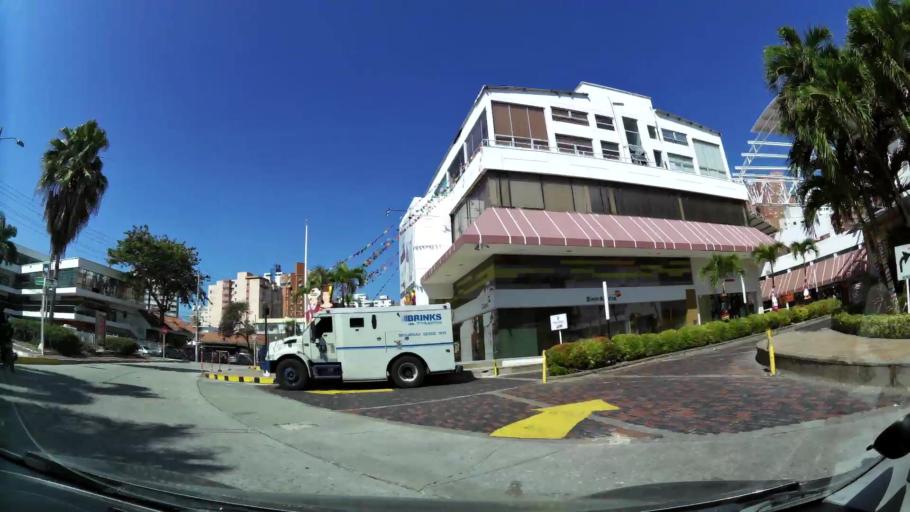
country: CO
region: Atlantico
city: Barranquilla
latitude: 11.0043
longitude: -74.8072
